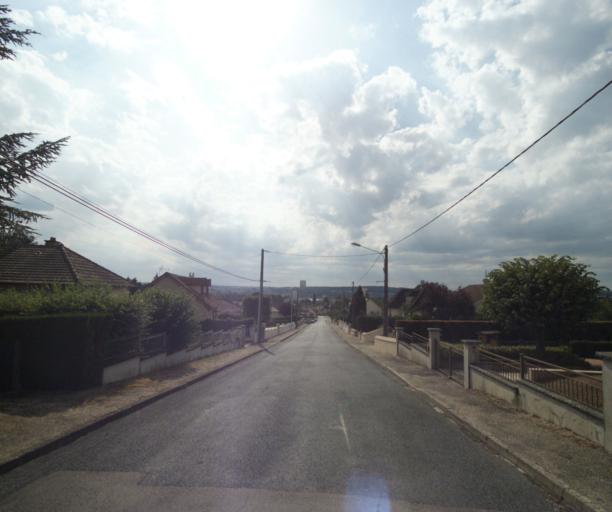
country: FR
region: Bourgogne
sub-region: Departement de Saone-et-Loire
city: Gueugnon
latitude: 46.6028
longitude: 4.0788
